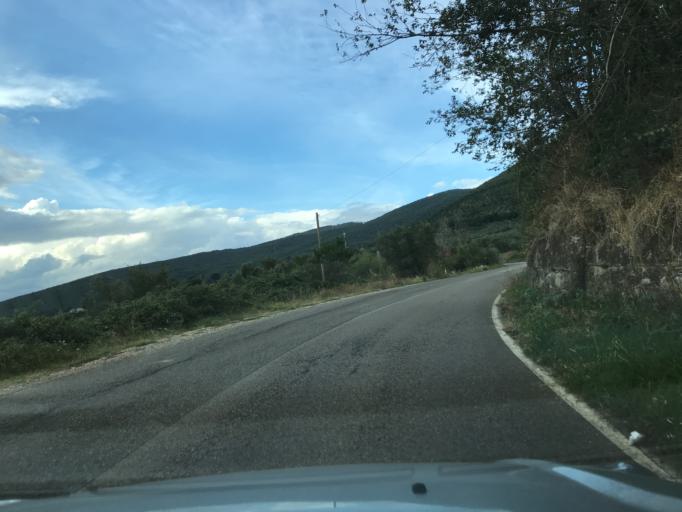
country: IT
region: Umbria
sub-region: Provincia di Terni
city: Montecchio
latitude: 42.6667
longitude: 12.2911
